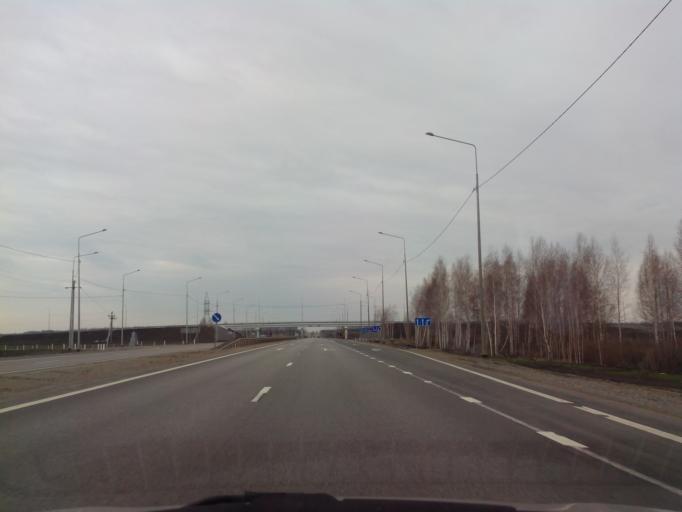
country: RU
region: Tambov
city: Zavoronezhskoye
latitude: 52.8863
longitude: 40.7153
